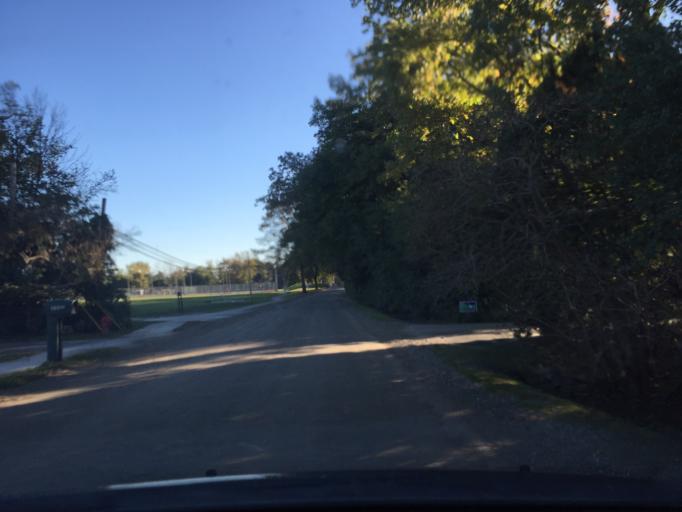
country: US
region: Michigan
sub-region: Oakland County
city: Franklin
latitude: 42.5612
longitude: -83.2949
